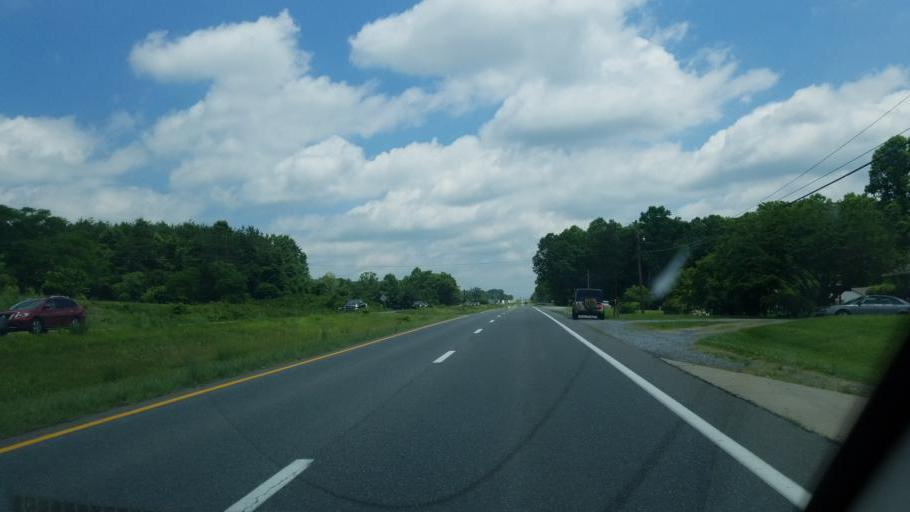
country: US
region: Virginia
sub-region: Campbell County
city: Rustburg
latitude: 37.2656
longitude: -79.1781
